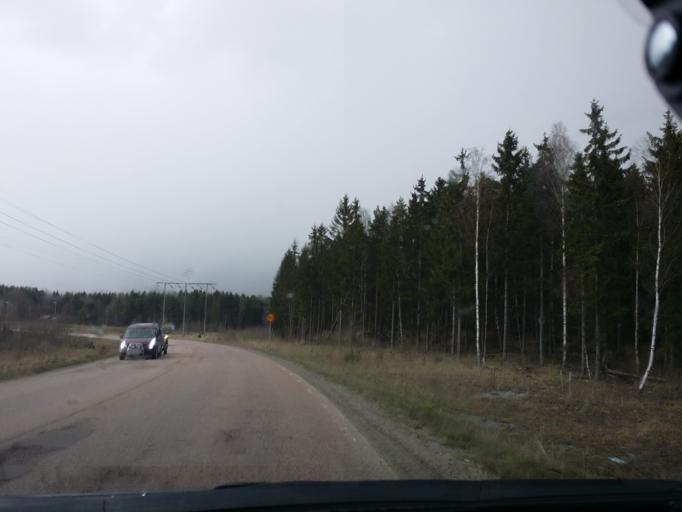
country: SE
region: Uppsala
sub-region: Enkopings Kommun
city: Enkoping
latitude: 59.6414
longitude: 17.1448
